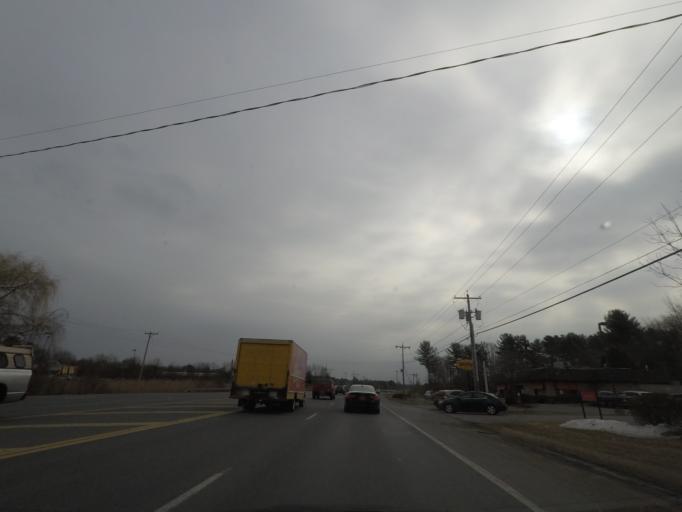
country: US
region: New York
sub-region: Warren County
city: Glens Falls
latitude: 43.3322
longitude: -73.6517
